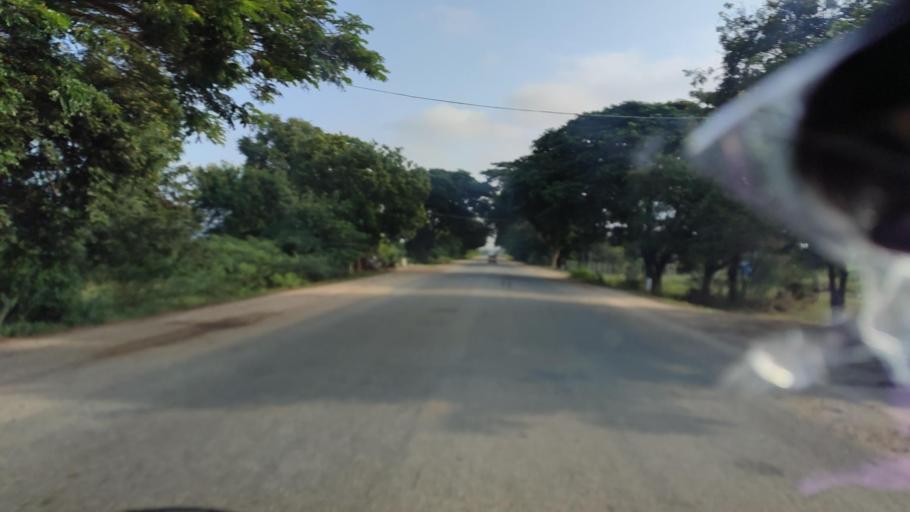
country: MM
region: Mandalay
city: Yamethin
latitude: 20.6973
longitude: 96.1678
